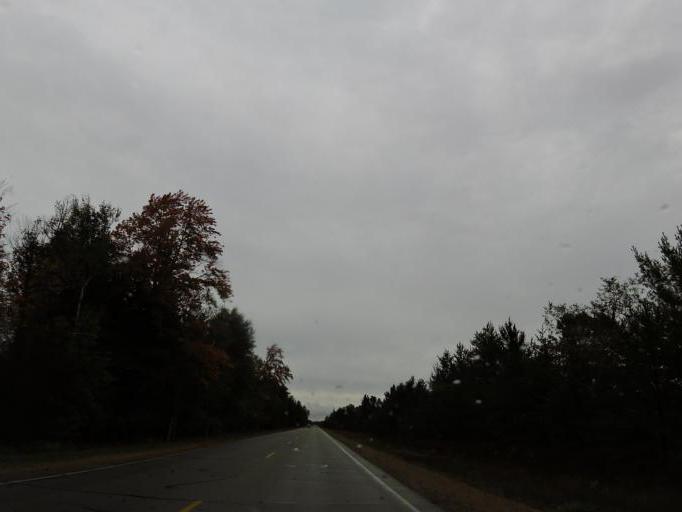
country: US
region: Michigan
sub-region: Roscommon County
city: Roscommon
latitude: 44.4418
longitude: -84.5152
